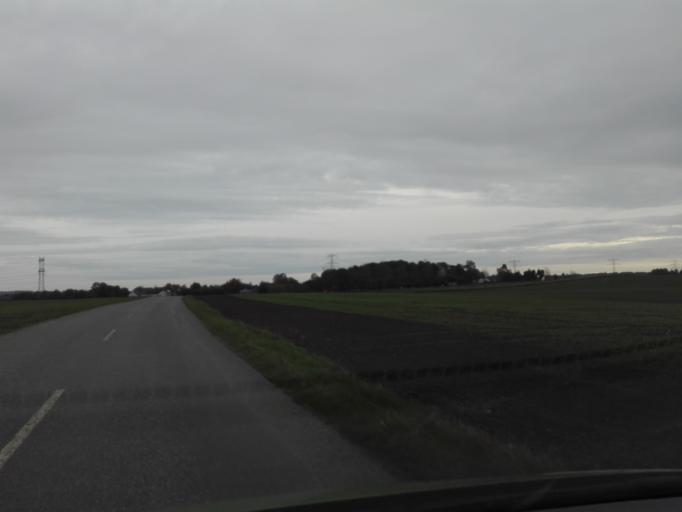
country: DK
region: Central Jutland
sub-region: Arhus Kommune
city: Tranbjerg
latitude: 56.0653
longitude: 10.1214
